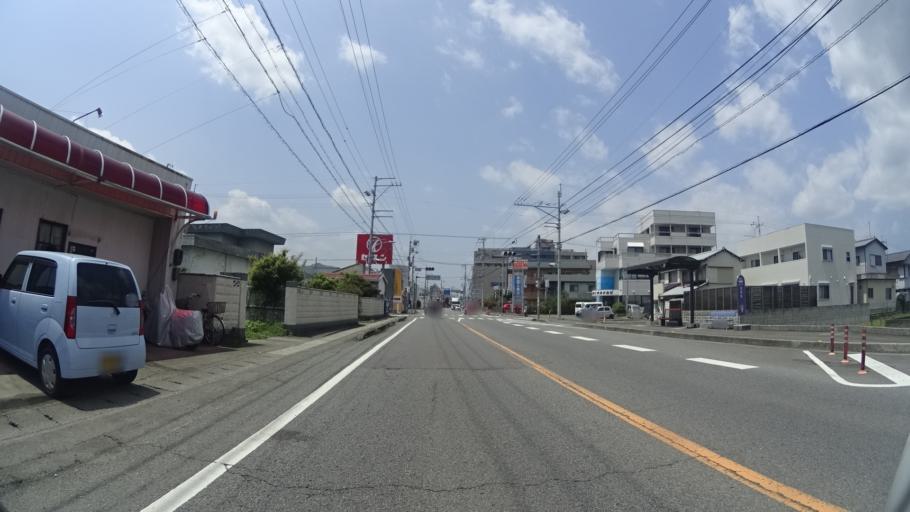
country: JP
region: Tokushima
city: Ishii
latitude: 34.0683
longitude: 134.4455
